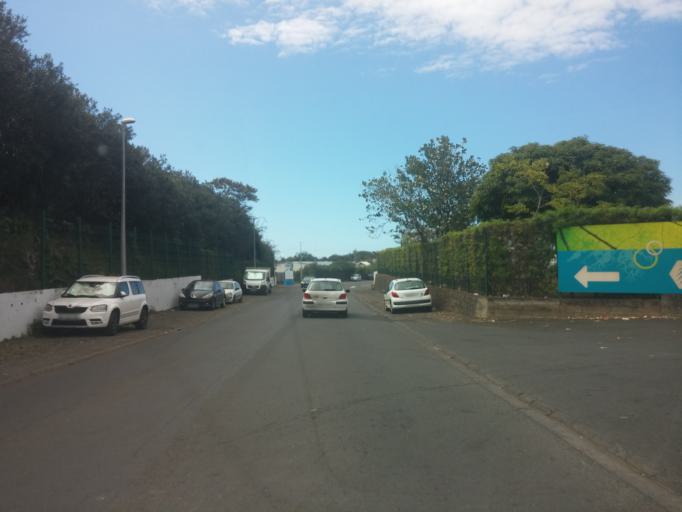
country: RE
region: Reunion
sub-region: Reunion
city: Sainte-Marie
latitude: -20.8991
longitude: 55.5313
